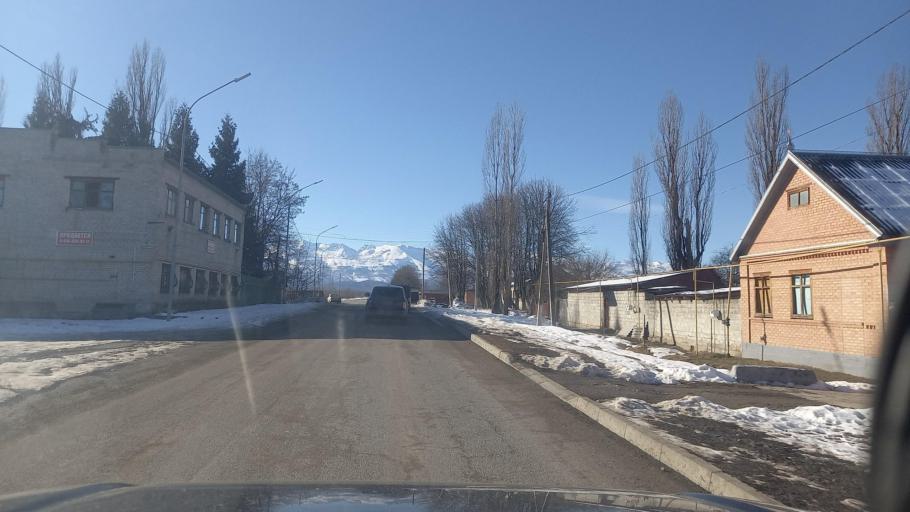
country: RU
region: North Ossetia
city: Chikola
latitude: 43.1861
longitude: 43.9001
